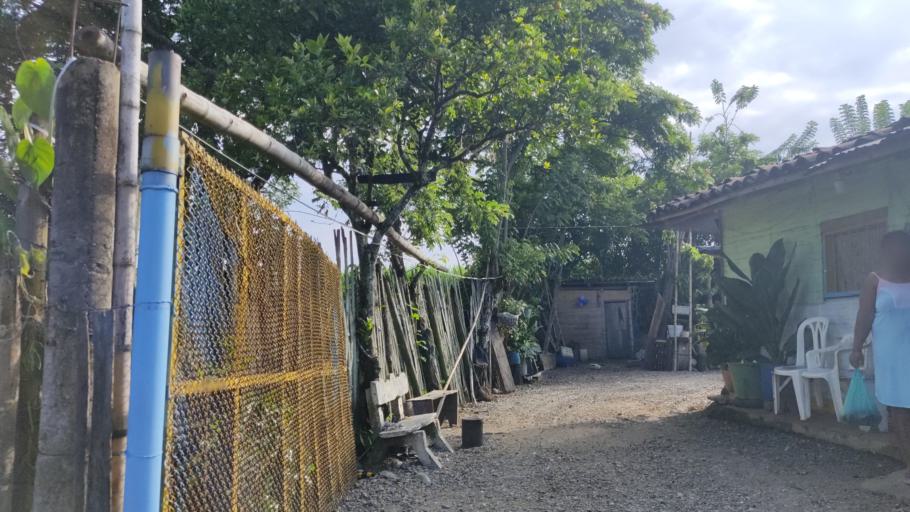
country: CO
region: Valle del Cauca
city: Jamundi
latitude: 3.1305
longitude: -76.5559
